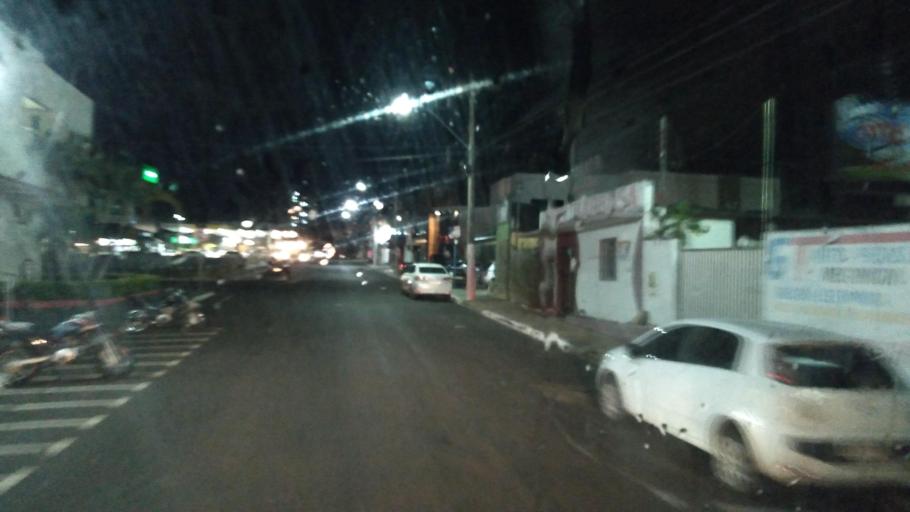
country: BR
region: Goias
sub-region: Mineiros
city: Mineiros
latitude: -17.5667
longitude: -52.5606
